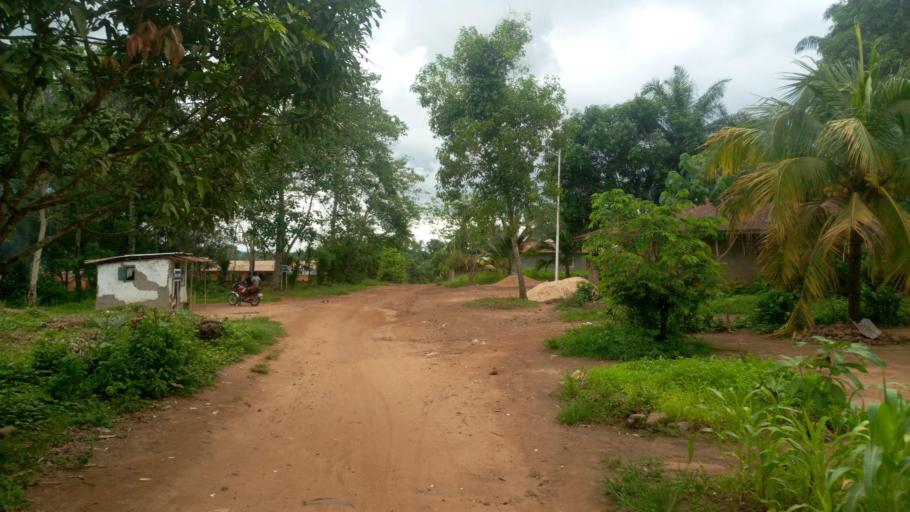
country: SL
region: Southern Province
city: Mogbwemo
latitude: 7.6004
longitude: -12.1753
